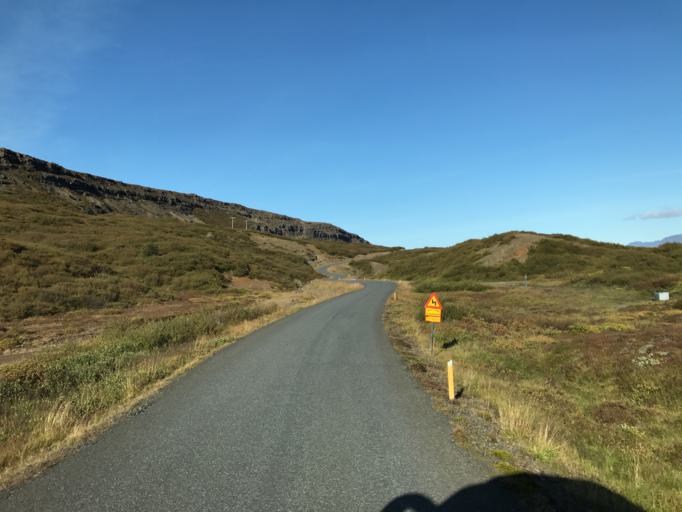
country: IS
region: South
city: Hveragerdi
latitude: 64.1537
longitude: -21.2546
